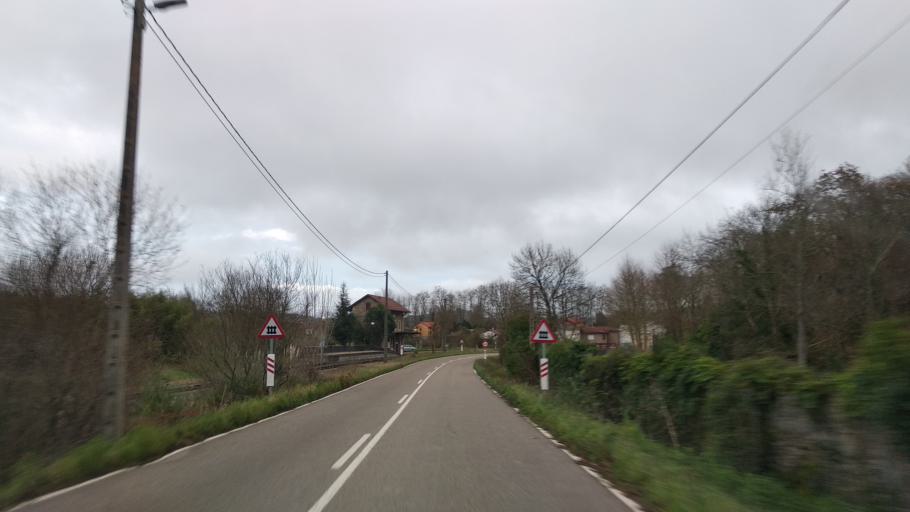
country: ES
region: Cantabria
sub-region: Provincia de Cantabria
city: Entrambasaguas
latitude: 43.4105
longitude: -3.7048
